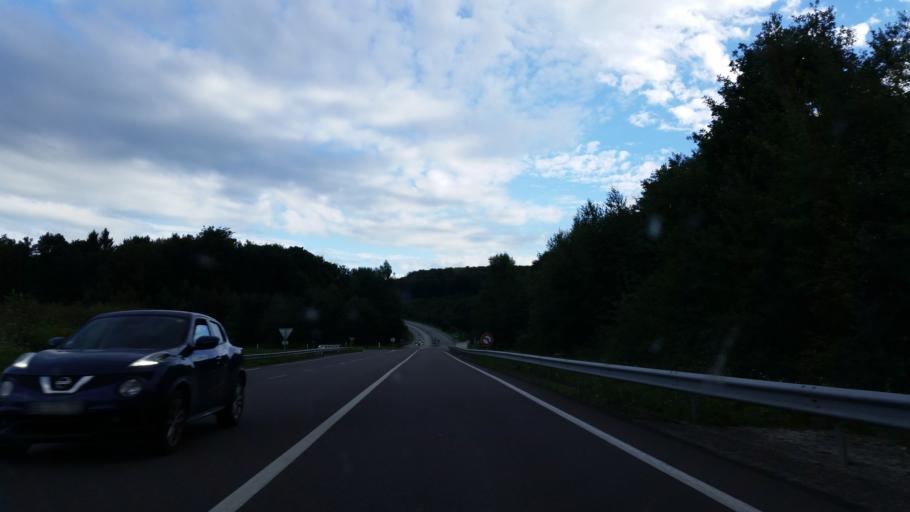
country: FR
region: Franche-Comte
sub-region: Departement de la Haute-Saone
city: Fougerolles
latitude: 47.8669
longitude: 6.3816
